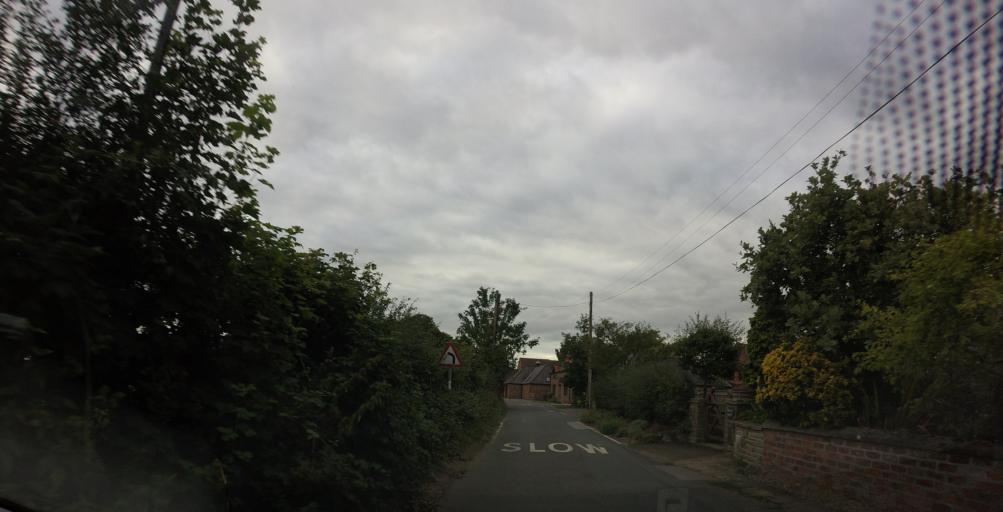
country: GB
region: England
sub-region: City of York
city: Nether Poppleton
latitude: 53.9783
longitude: -1.1536
